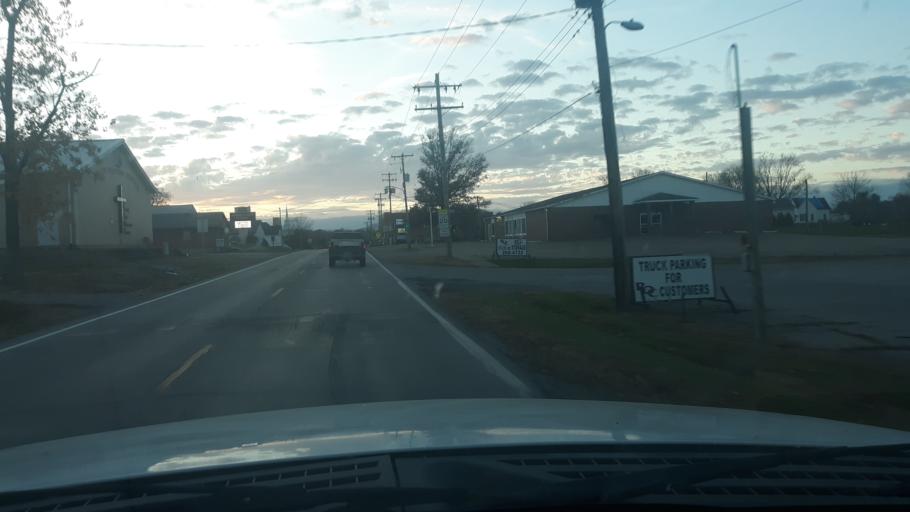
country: US
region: Illinois
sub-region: Saline County
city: Harrisburg
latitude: 37.8408
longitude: -88.6100
